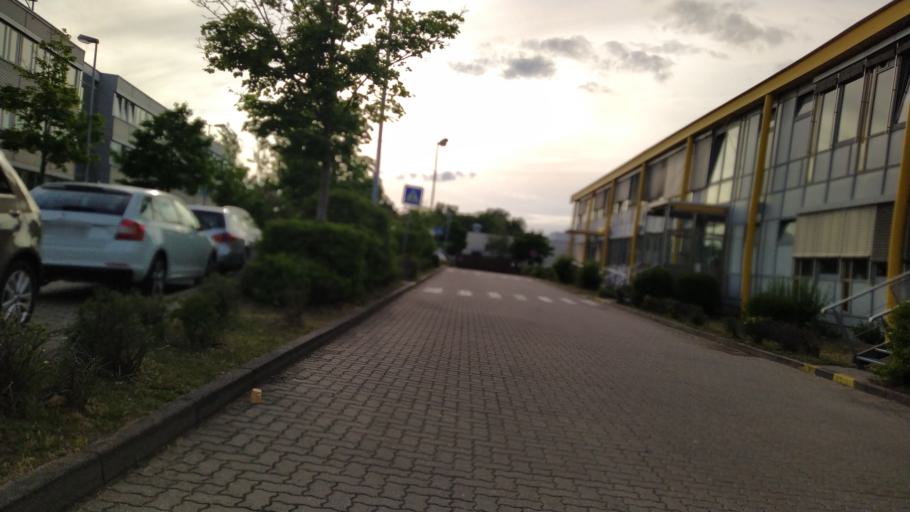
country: DE
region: Hamburg
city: Altona
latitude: 53.4826
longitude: 9.9044
